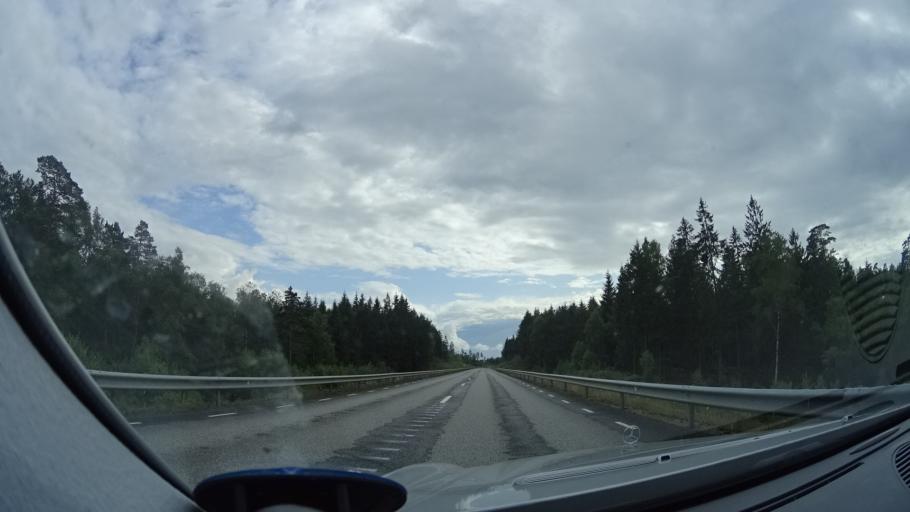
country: SE
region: Blekinge
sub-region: Karlshamns Kommun
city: Svangsta
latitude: 56.2804
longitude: 14.8664
